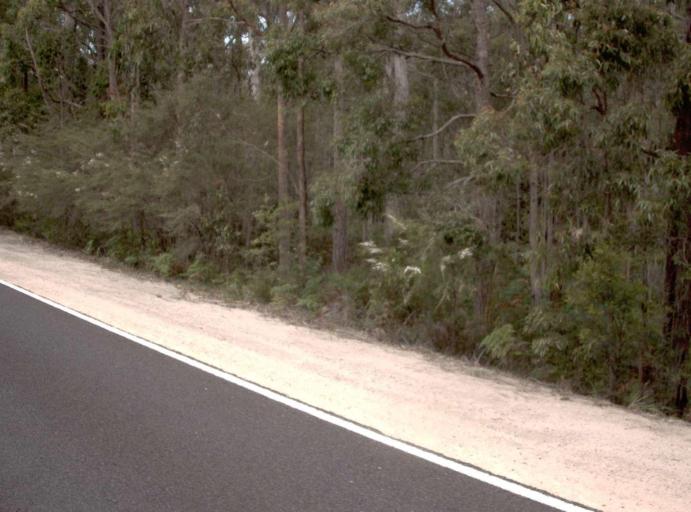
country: AU
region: New South Wales
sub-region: Bega Valley
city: Eden
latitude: -37.3988
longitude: 149.6717
